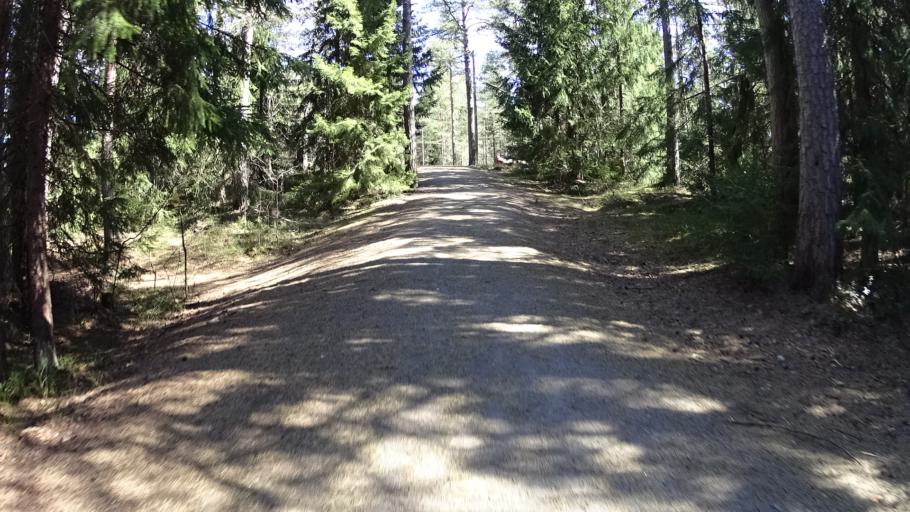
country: FI
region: Uusimaa
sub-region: Helsinki
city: Espoo
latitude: 60.1942
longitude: 24.6068
